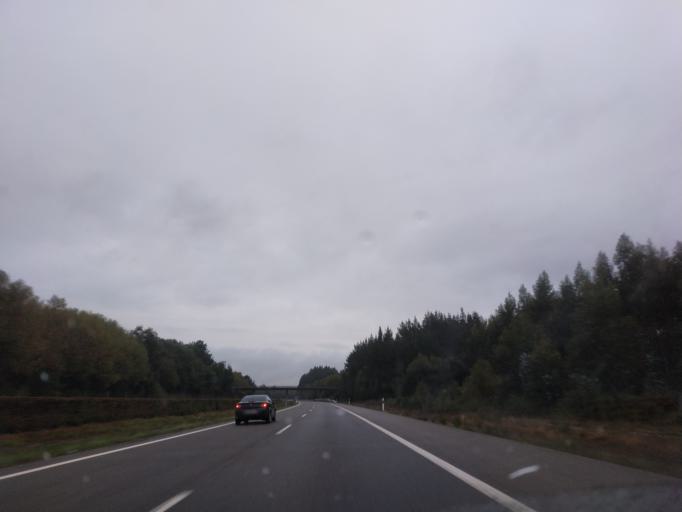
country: ES
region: Galicia
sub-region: Provincia de Lugo
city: Begonte
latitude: 43.1414
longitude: -7.6483
